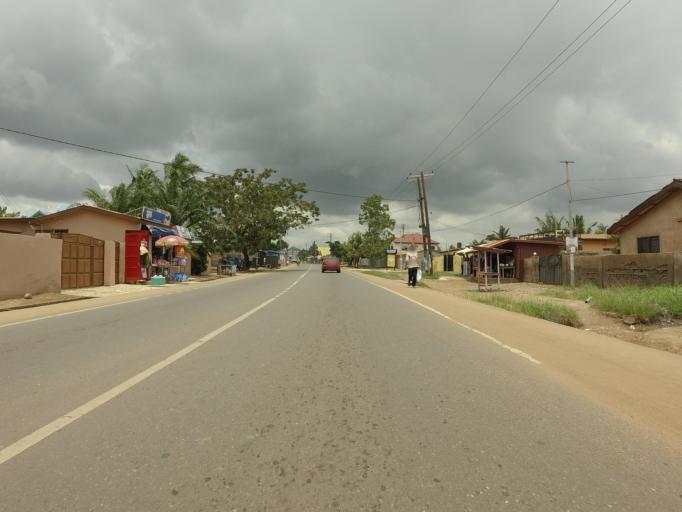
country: GH
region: Greater Accra
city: Medina Estates
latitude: 5.6820
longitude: -0.1504
